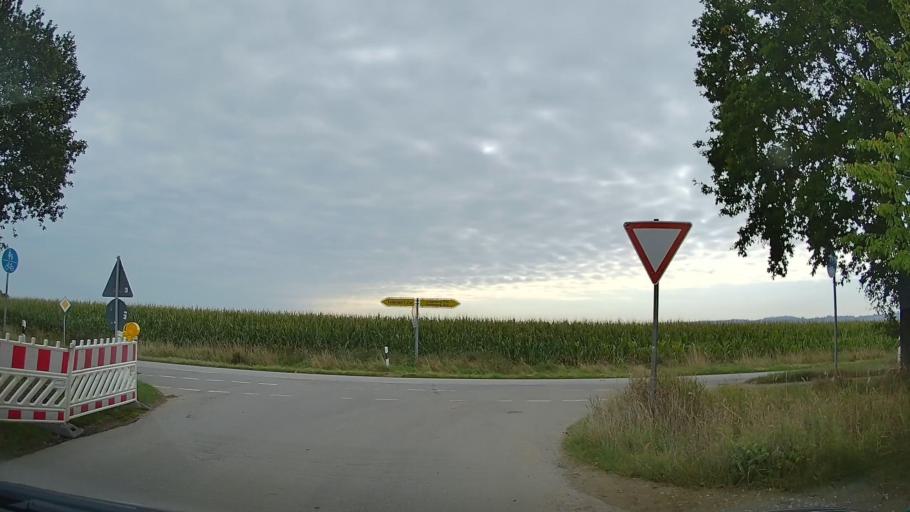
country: DE
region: Schleswig-Holstein
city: Panker
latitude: 54.3668
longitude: 10.5424
